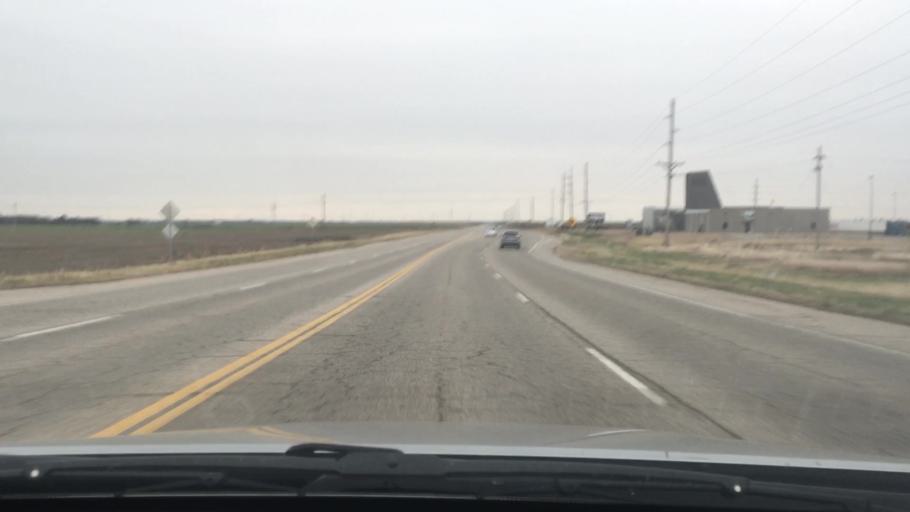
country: US
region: Kansas
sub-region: Reno County
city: Hutchinson
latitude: 38.0459
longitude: -97.8668
